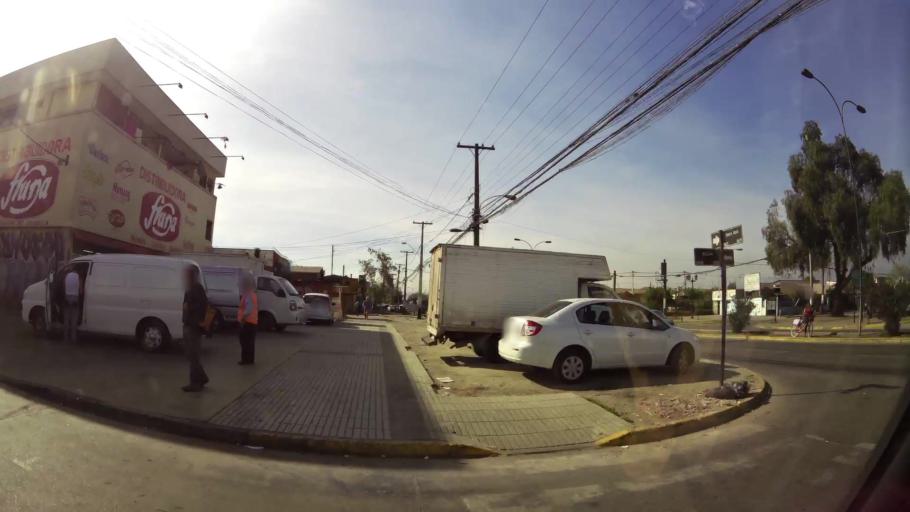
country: CL
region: Santiago Metropolitan
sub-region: Provincia de Santiago
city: La Pintana
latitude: -33.5397
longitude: -70.6345
